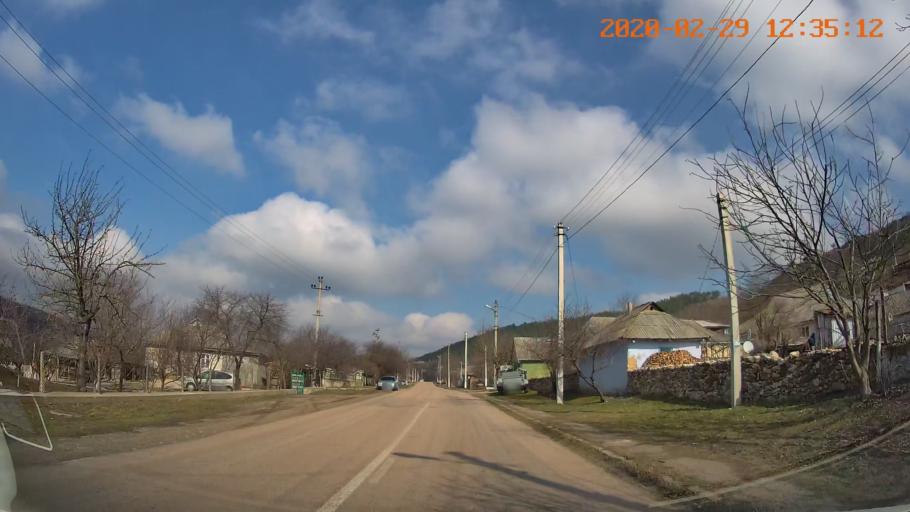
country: MD
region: Telenesti
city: Camenca
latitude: 48.0452
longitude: 28.7192
